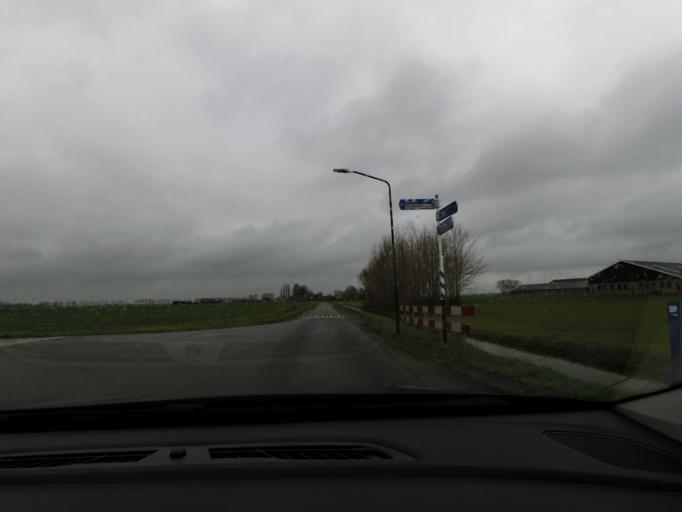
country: NL
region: North Brabant
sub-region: Gemeente Waalwijk
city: Waalwijk
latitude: 51.7513
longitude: 5.0573
